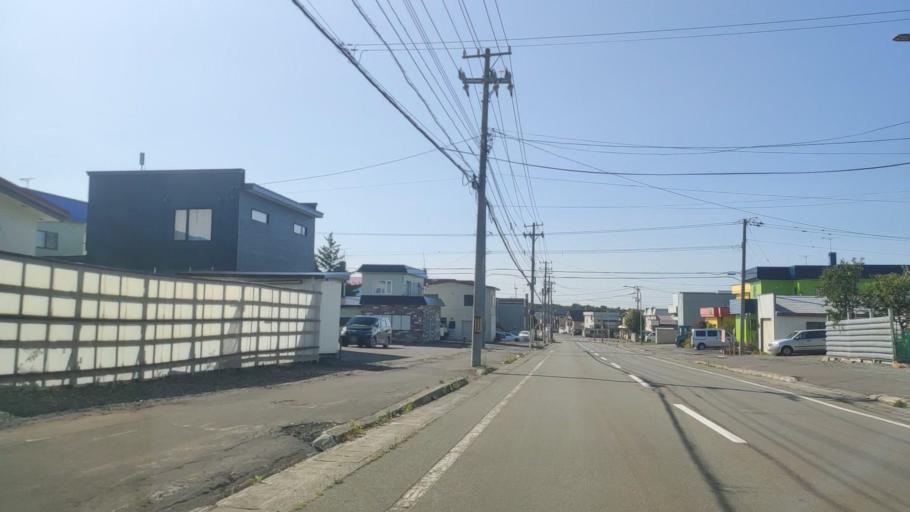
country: JP
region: Hokkaido
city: Wakkanai
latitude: 45.3890
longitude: 141.7215
